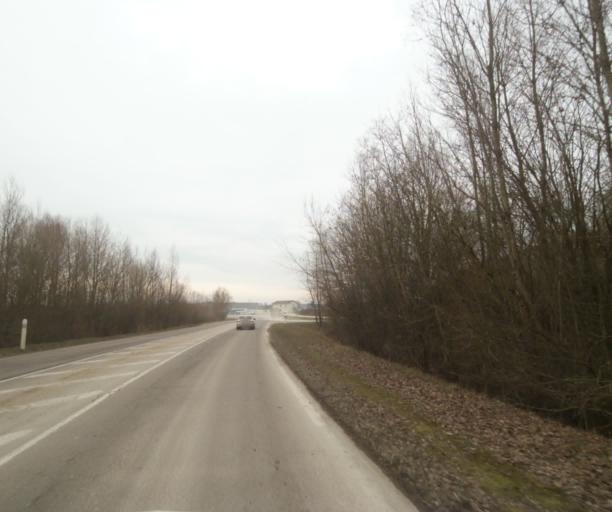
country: FR
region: Champagne-Ardenne
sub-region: Departement de la Haute-Marne
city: Villiers-en-Lieu
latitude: 48.6442
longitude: 4.9084
